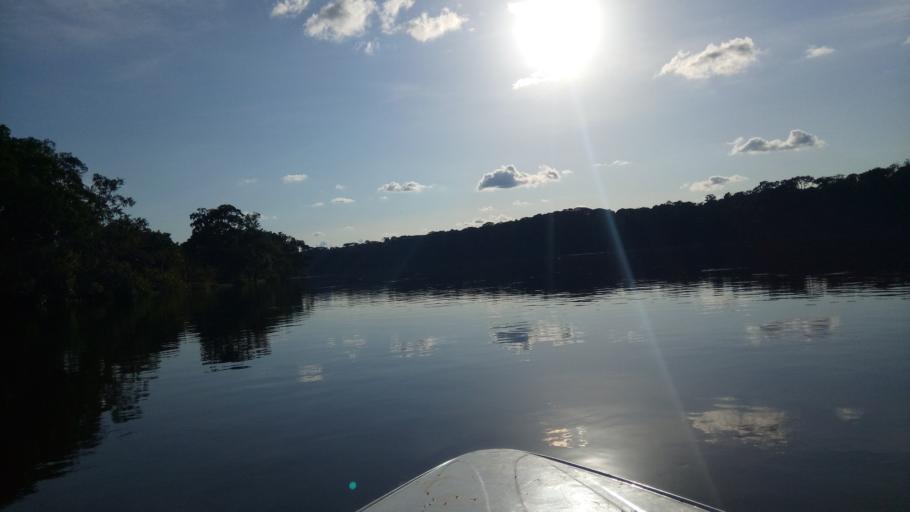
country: CD
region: Eastern Province
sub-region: Sous-Region de la Tshopo
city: Yangambi
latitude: 0.2554
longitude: 24.0577
